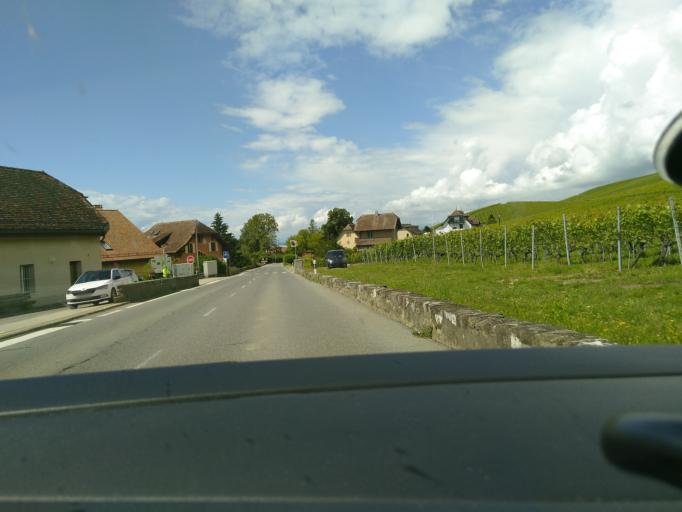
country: CH
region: Vaud
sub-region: Nyon District
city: Perroy
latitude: 46.4811
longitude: 6.3735
